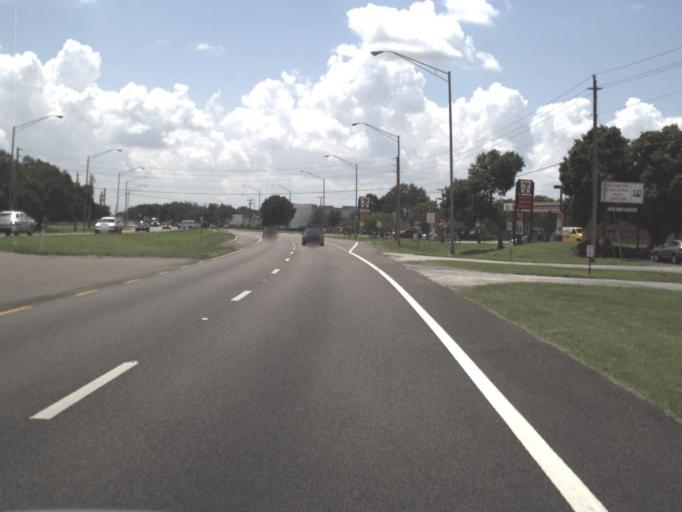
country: US
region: Florida
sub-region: Hillsborough County
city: East Lake-Orient Park
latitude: 27.9621
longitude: -82.3599
